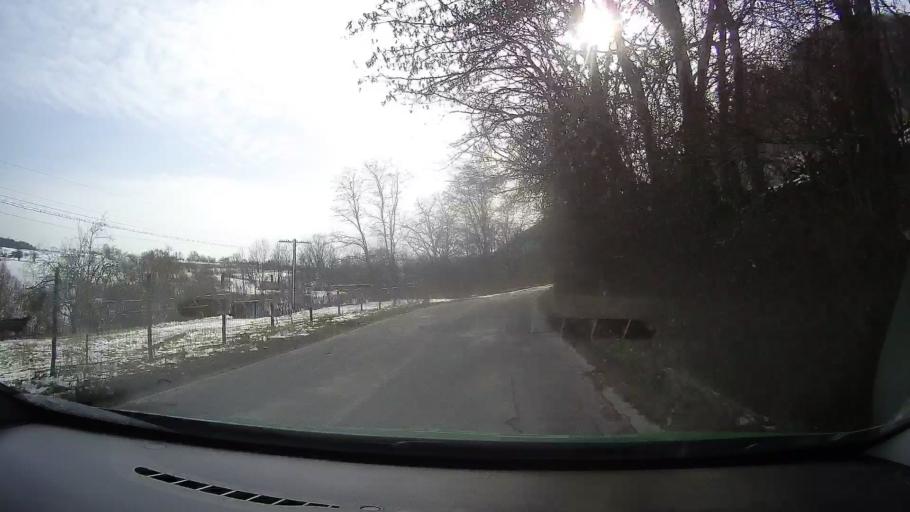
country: RO
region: Mures
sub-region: Municipiul Sighisoara
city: Sighisoara
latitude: 46.2007
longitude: 24.7693
